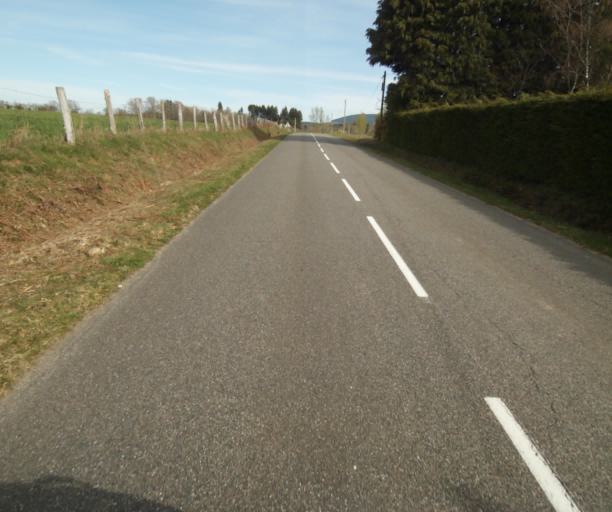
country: FR
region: Limousin
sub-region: Departement de la Correze
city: Correze
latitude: 45.4070
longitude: 1.8267
